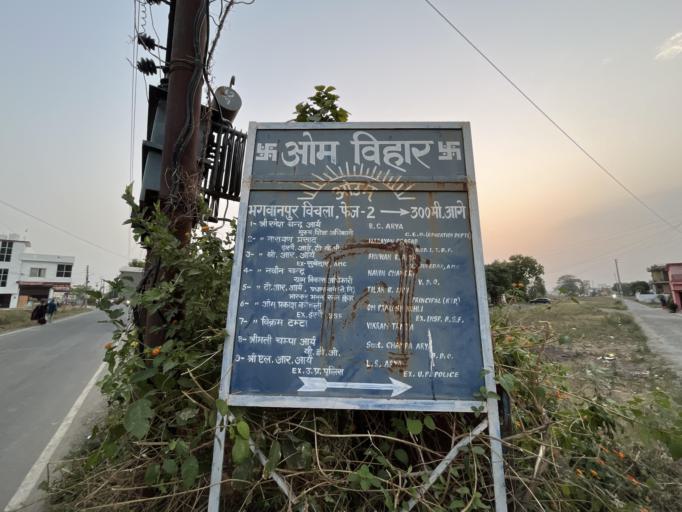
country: IN
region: Uttarakhand
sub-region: Naini Tal
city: Haldwani
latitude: 29.2205
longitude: 79.4763
